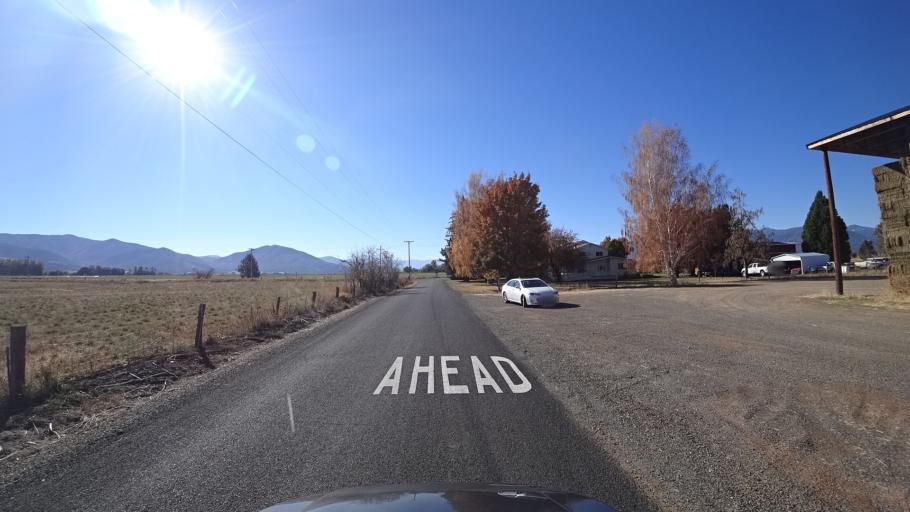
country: US
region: California
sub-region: Siskiyou County
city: Yreka
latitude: 41.5715
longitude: -122.8540
